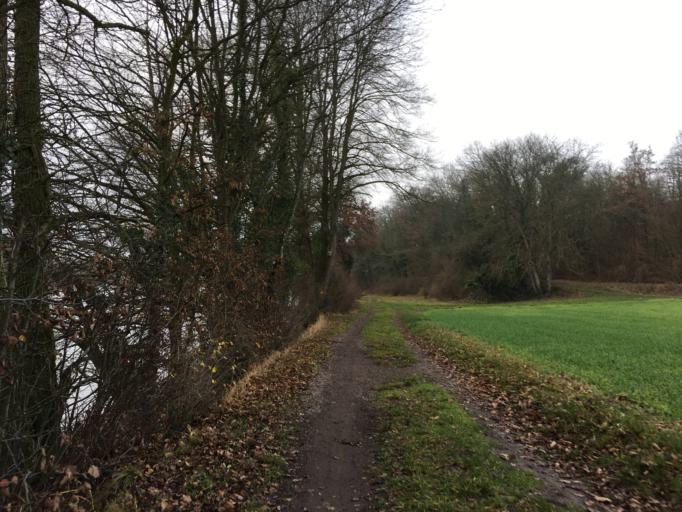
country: CH
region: Aargau
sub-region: Bezirk Zurzach
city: Bad Zurzach
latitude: 47.5786
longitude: 8.3179
